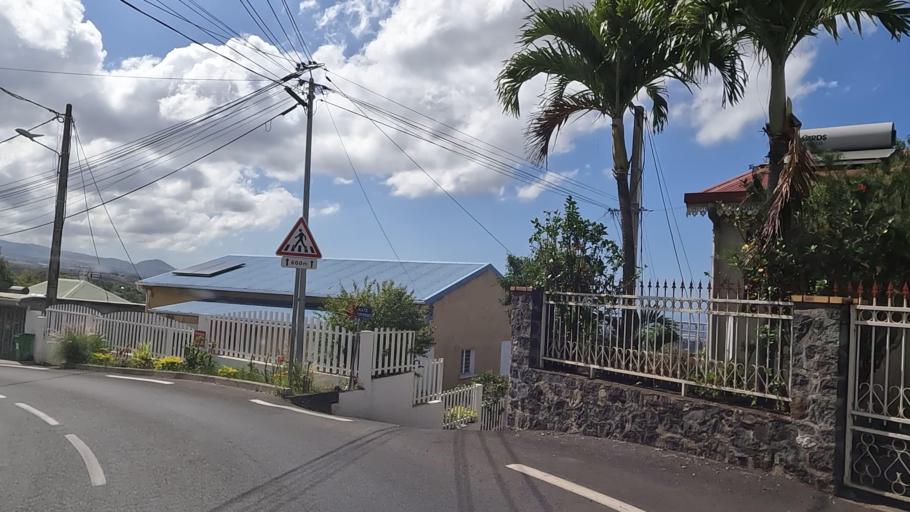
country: RE
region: Reunion
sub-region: Reunion
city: L'Entre-Deux
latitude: -21.2588
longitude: 55.4416
